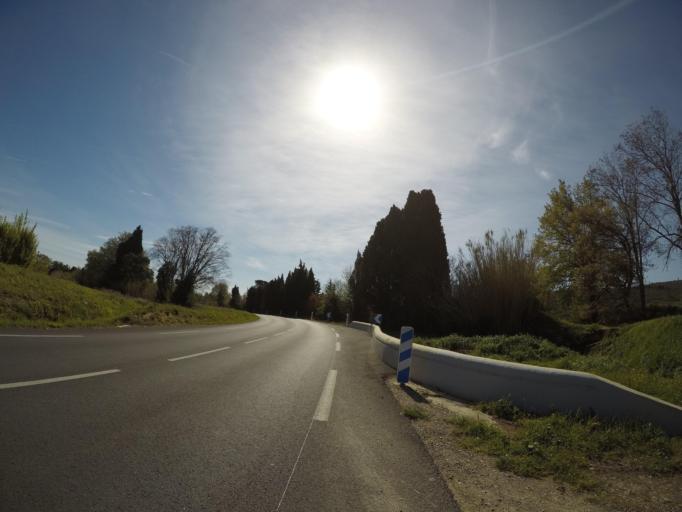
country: FR
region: Languedoc-Roussillon
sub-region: Departement des Pyrenees-Orientales
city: Millas
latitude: 42.6464
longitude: 2.7087
